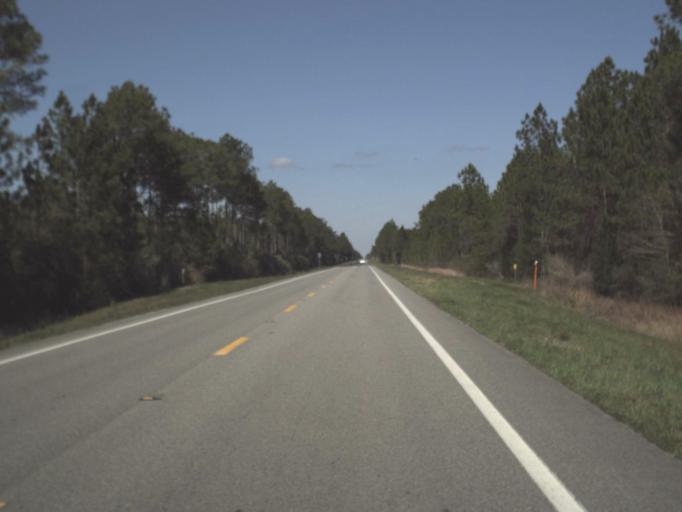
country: US
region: Florida
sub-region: Gulf County
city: Port Saint Joe
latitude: 29.8943
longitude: -85.2144
